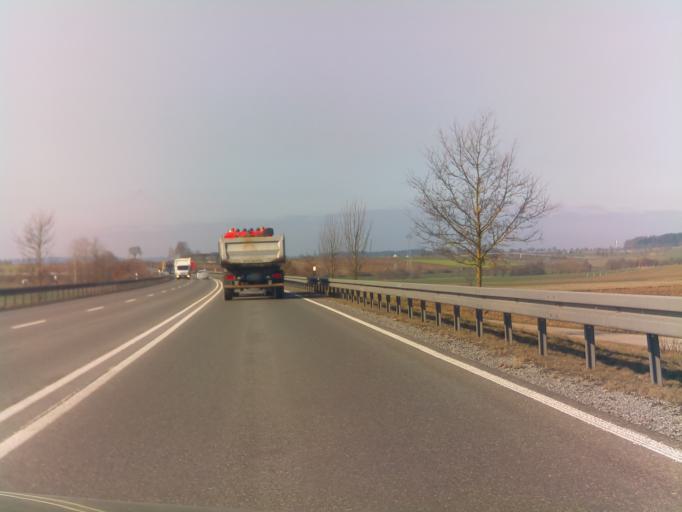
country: DE
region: Baden-Wuerttemberg
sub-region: Regierungsbezirk Stuttgart
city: Bondorf
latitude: 48.5073
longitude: 8.8096
